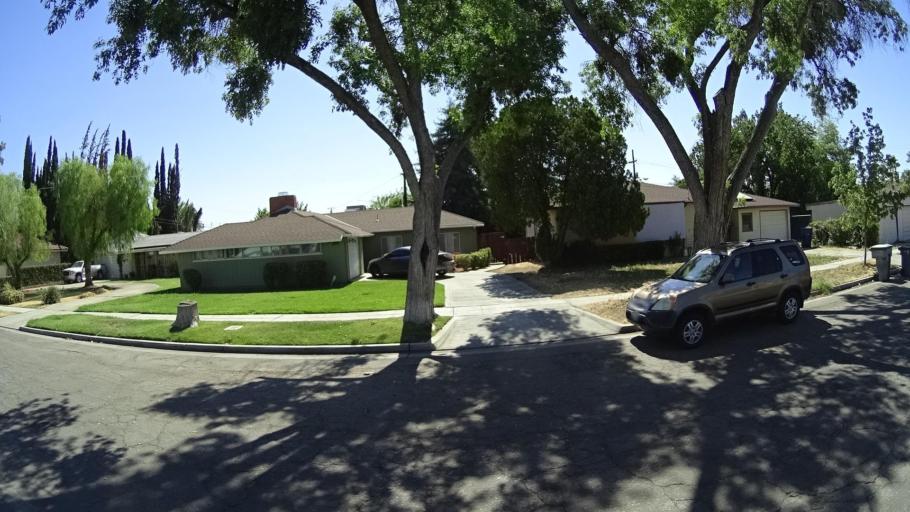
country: US
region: California
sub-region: Fresno County
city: Fresno
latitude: 36.7655
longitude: -119.8200
